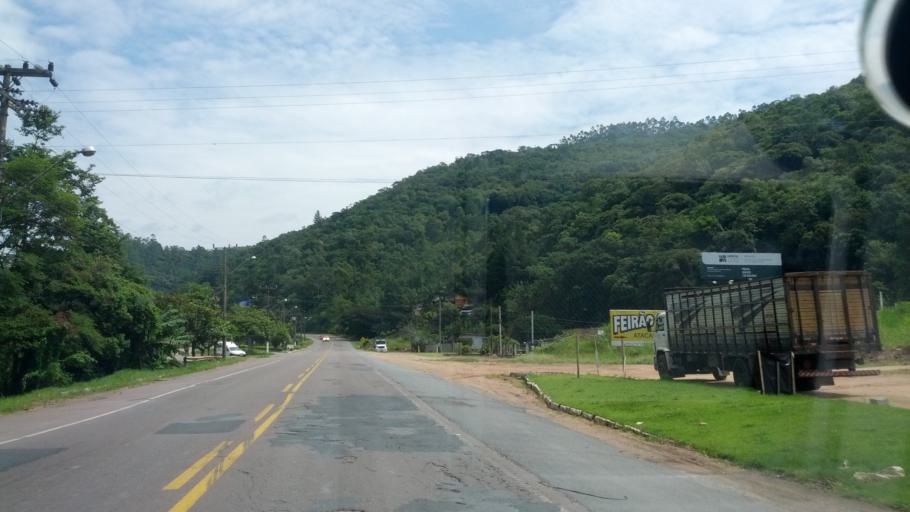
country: BR
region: Santa Catarina
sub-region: Ibirama
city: Ibirama
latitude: -27.0815
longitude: -49.4841
